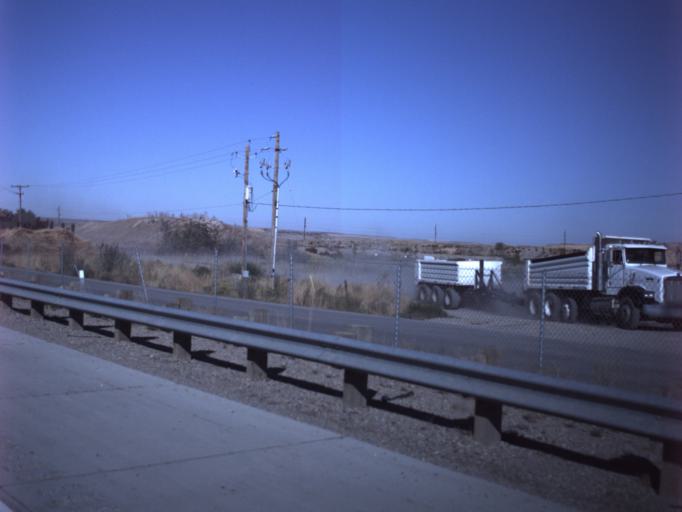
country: US
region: Utah
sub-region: Salt Lake County
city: West Valley City
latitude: 40.7256
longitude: -112.0373
